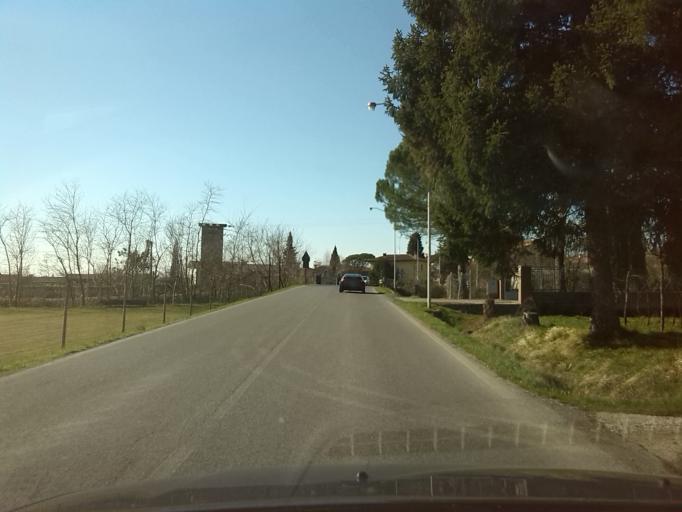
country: IT
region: Friuli Venezia Giulia
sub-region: Provincia di Udine
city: Faedis
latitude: 46.1276
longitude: 13.3650
